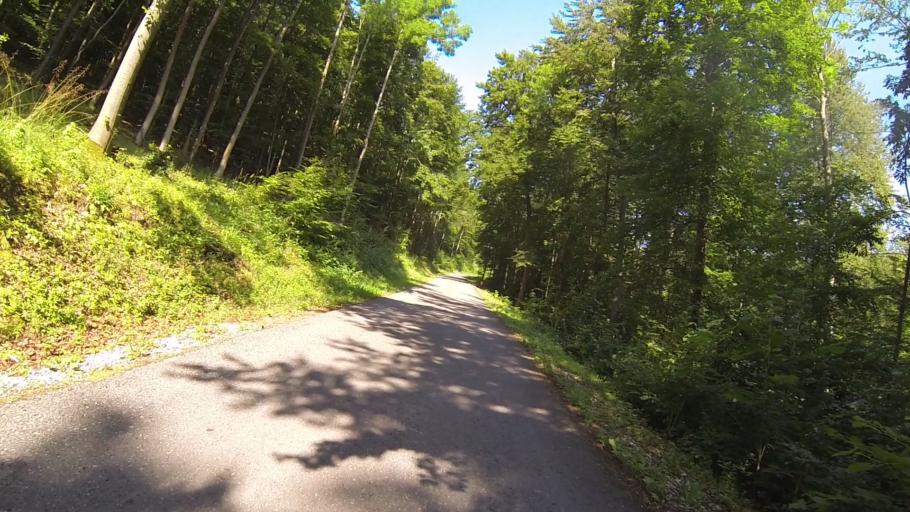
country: DE
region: Baden-Wuerttemberg
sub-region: Regierungsbezirk Stuttgart
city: Oberkochen
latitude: 48.7830
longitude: 10.0925
